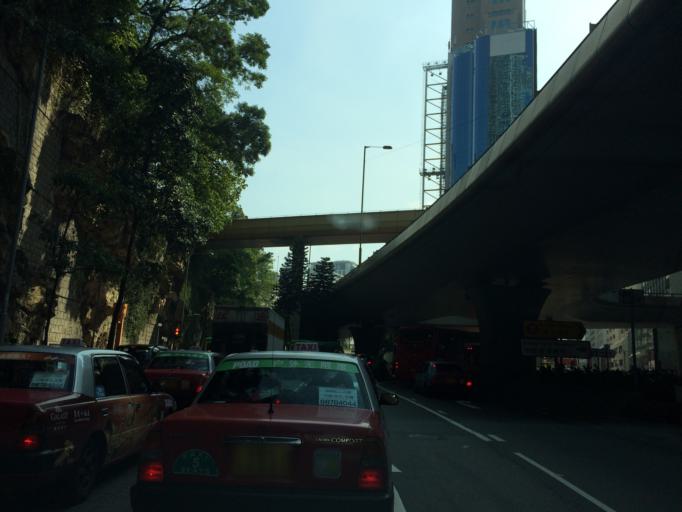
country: HK
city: Hong Kong
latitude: 22.3006
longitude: 114.1683
